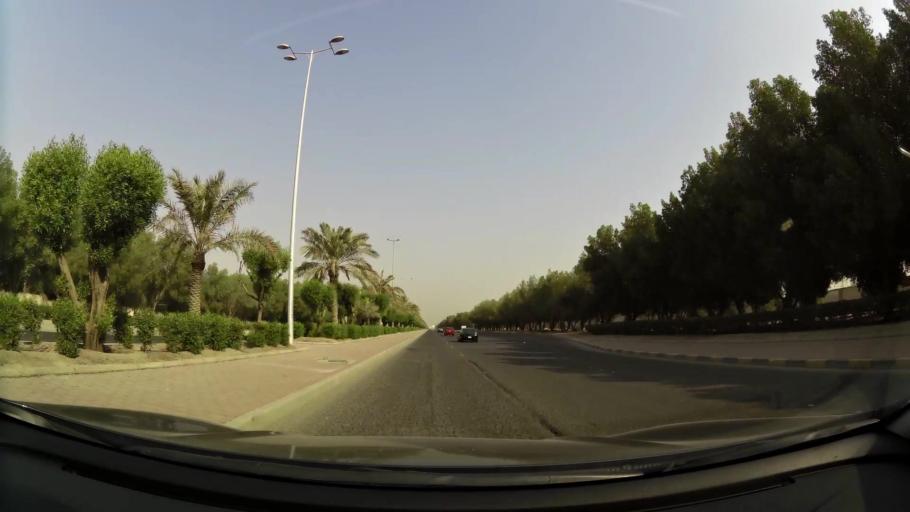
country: KW
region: Al Asimah
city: Ar Rabiyah
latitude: 29.2989
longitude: 47.8322
